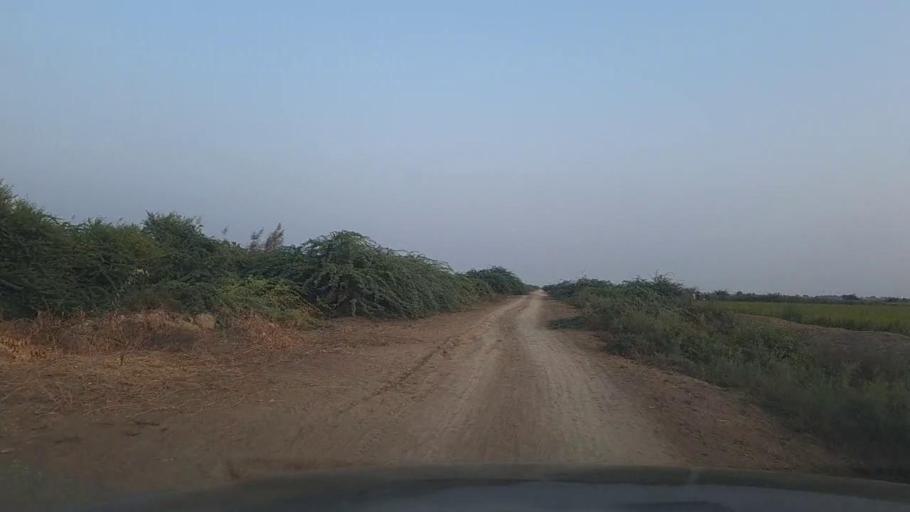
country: PK
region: Sindh
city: Mirpur Batoro
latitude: 24.5444
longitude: 68.3925
